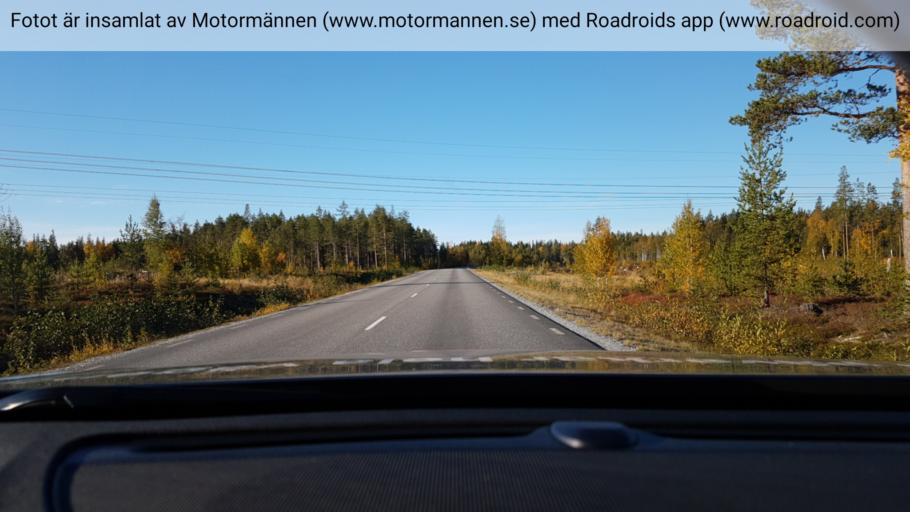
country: SE
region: Norrbotten
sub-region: Pitea Kommun
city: Roknas
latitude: 65.3470
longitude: 21.0106
